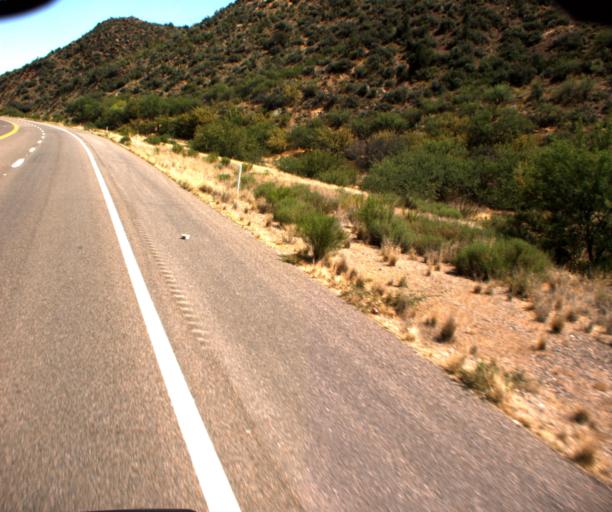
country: US
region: Arizona
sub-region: Gila County
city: Claypool
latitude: 33.4626
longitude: -110.8500
